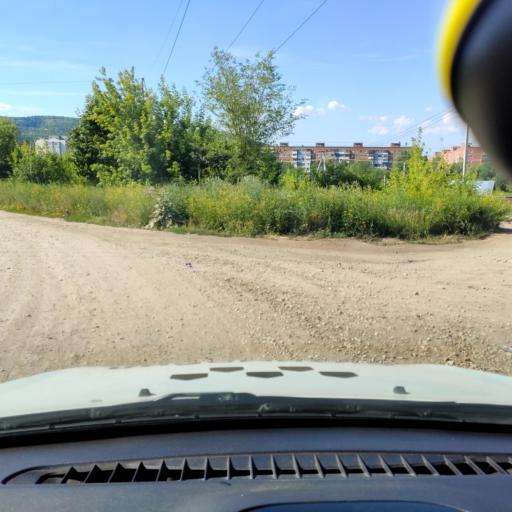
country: RU
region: Samara
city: Zhigulevsk
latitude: 53.3997
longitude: 49.5235
